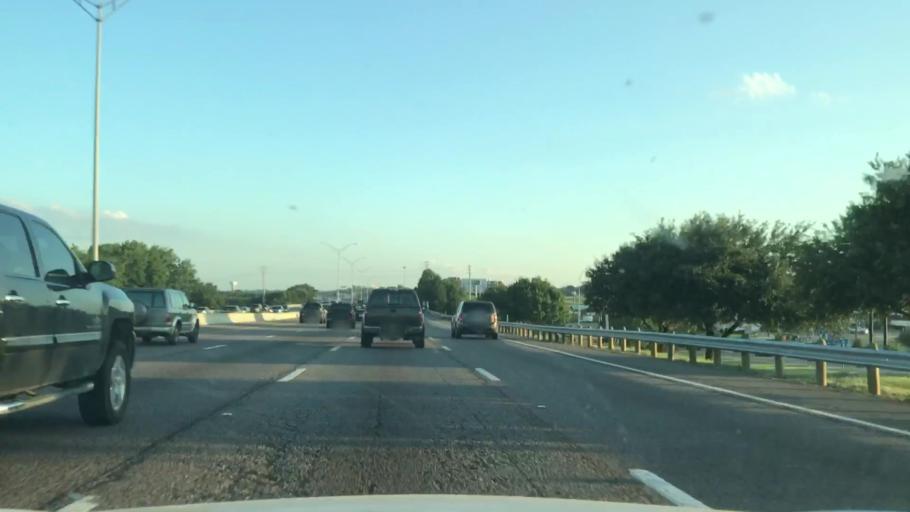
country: US
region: Texas
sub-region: Dallas County
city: Mesquite
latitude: 32.7705
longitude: -96.6233
